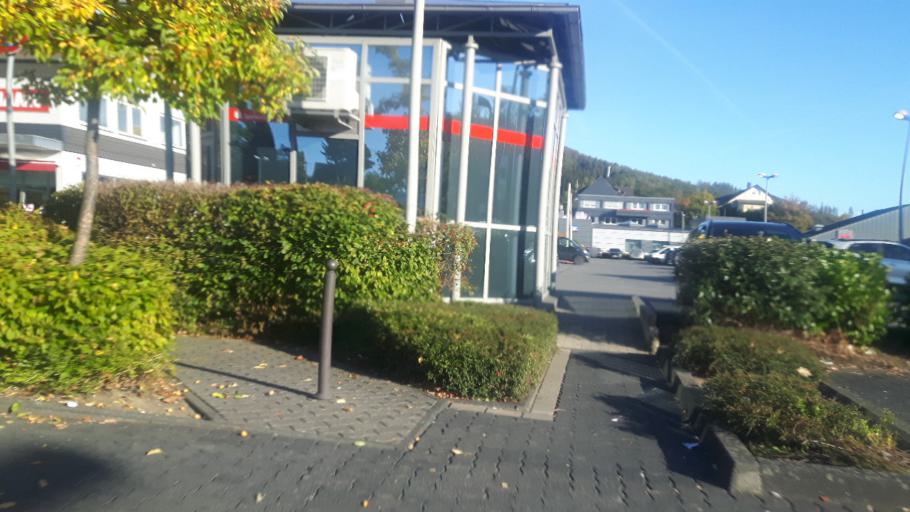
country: DE
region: Rheinland-Pfalz
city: Betzdorf
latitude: 50.7916
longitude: 7.8677
